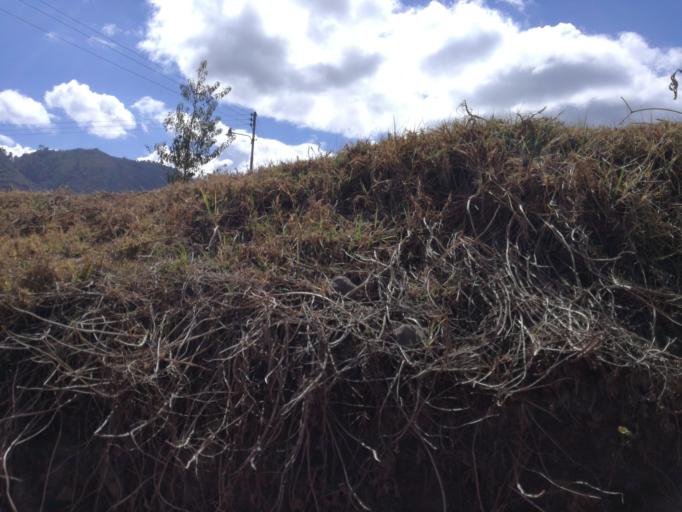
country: GT
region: Quetzaltenango
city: Almolonga
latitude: 14.7878
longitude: -91.5450
